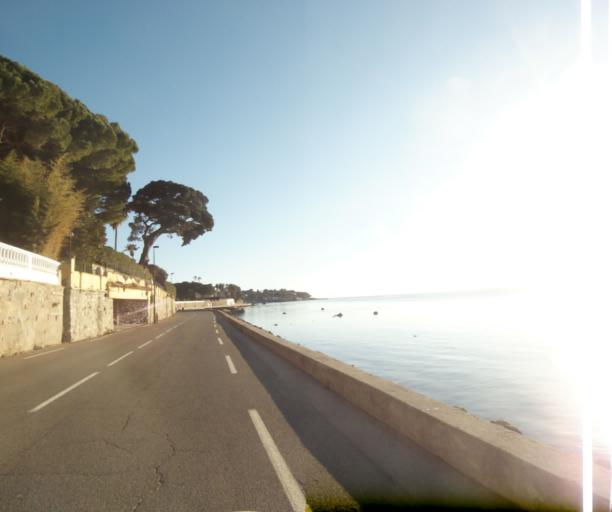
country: FR
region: Provence-Alpes-Cote d'Azur
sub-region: Departement des Alpes-Maritimes
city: Antibes
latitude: 43.5591
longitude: 7.1218
